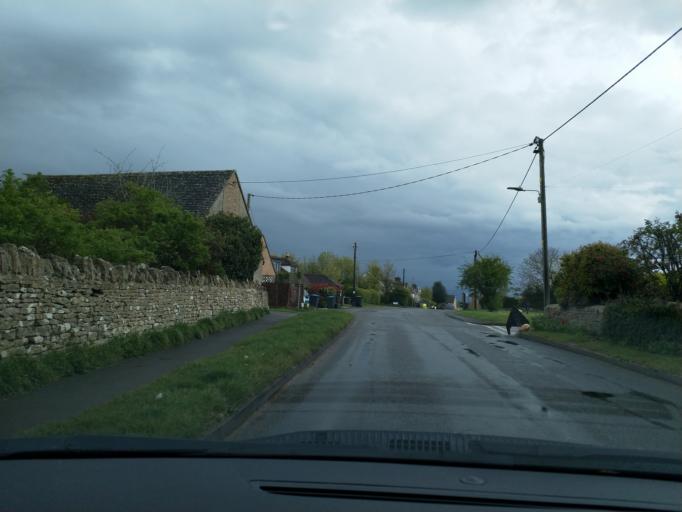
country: GB
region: England
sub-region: Oxfordshire
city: North Leigh
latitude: 51.8138
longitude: -1.4413
